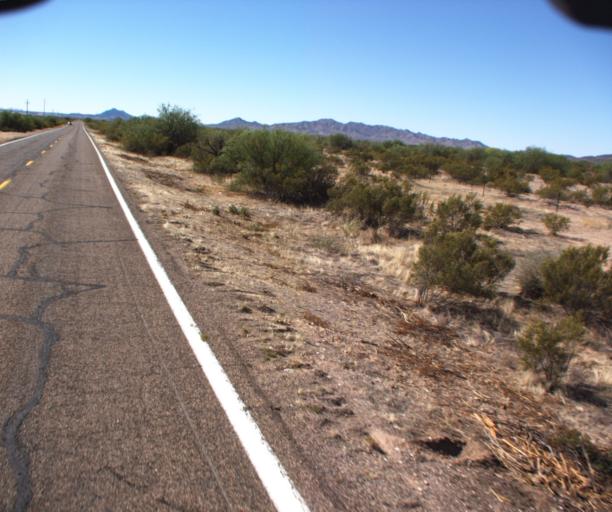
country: US
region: Arizona
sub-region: Pima County
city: Ajo
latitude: 32.4784
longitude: -112.8783
